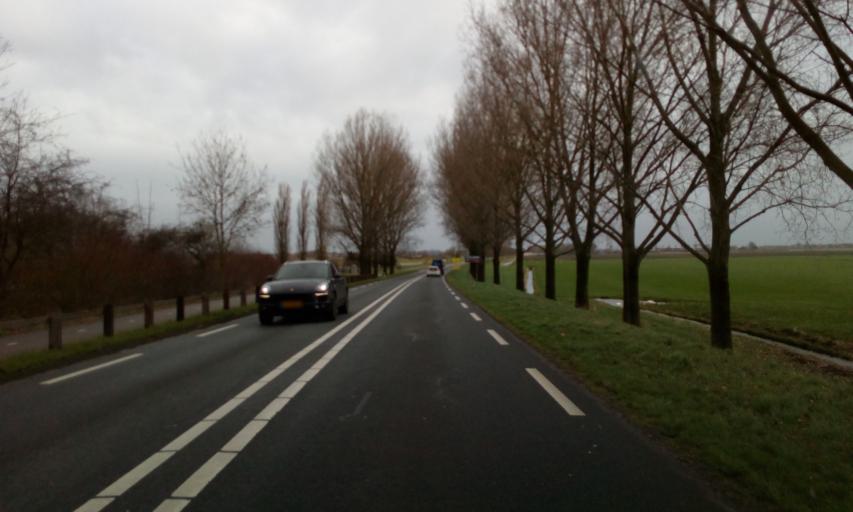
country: NL
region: South Holland
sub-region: Gemeente Nieuwkoop
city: Nieuwkoop
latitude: 52.1838
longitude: 4.7397
